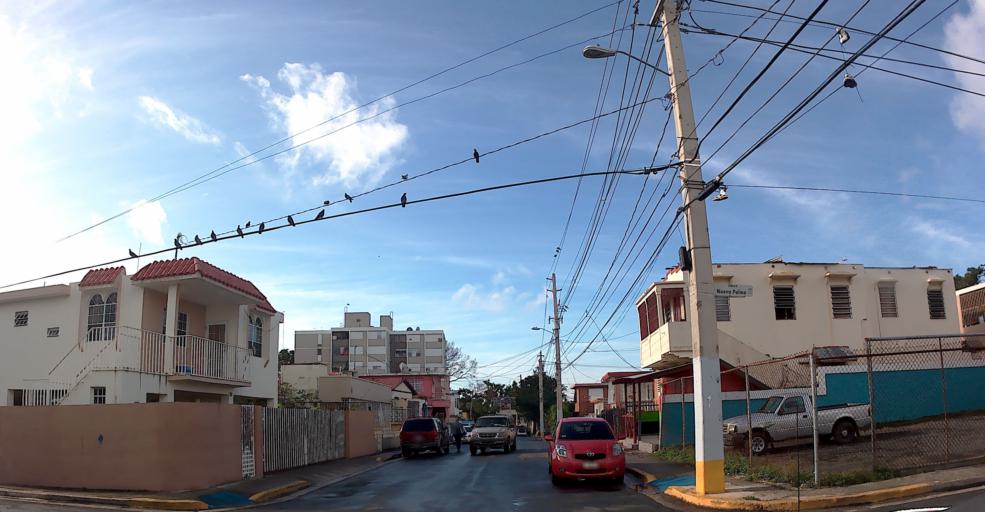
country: PR
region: San Juan
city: San Juan
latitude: 18.4453
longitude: -66.0766
